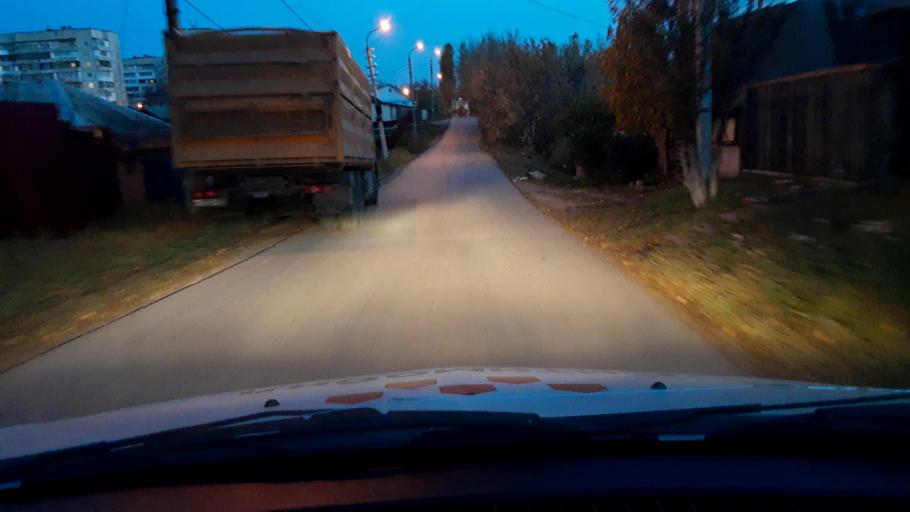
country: RU
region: Bashkortostan
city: Iglino
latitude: 54.7652
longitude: 56.2278
